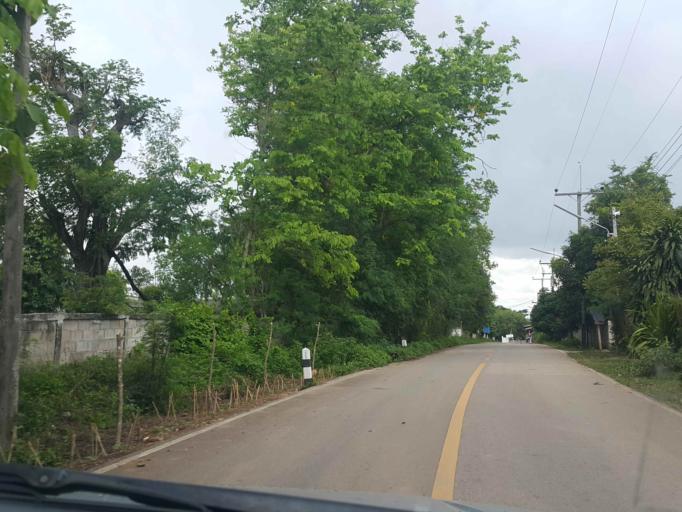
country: TH
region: Phayao
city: Dok Kham Tai
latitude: 19.0389
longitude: 99.9545
